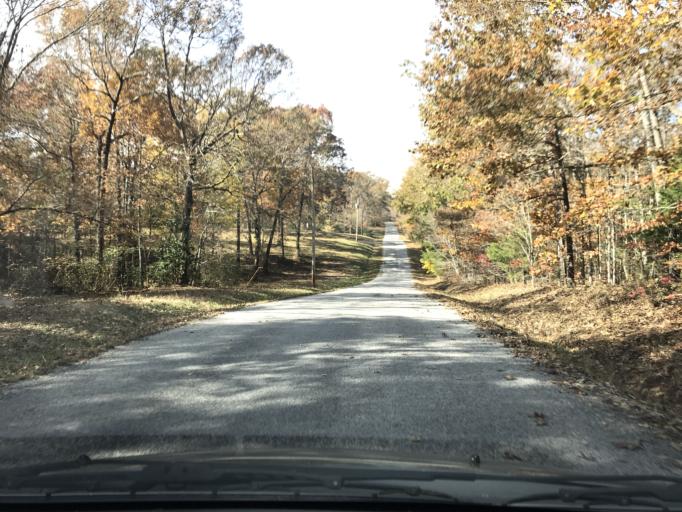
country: US
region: Tennessee
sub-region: Coffee County
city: Tullahoma
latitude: 35.4058
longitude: -86.1684
